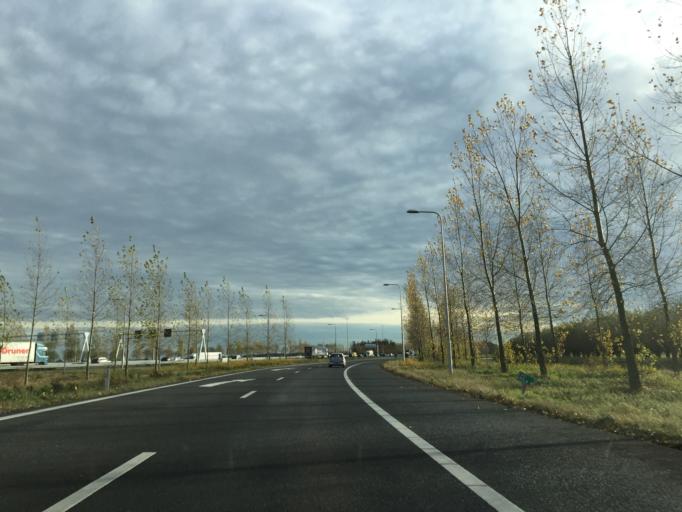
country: NL
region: Gelderland
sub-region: Gemeente Zaltbommel
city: Zaltbommel
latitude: 51.8543
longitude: 5.2292
